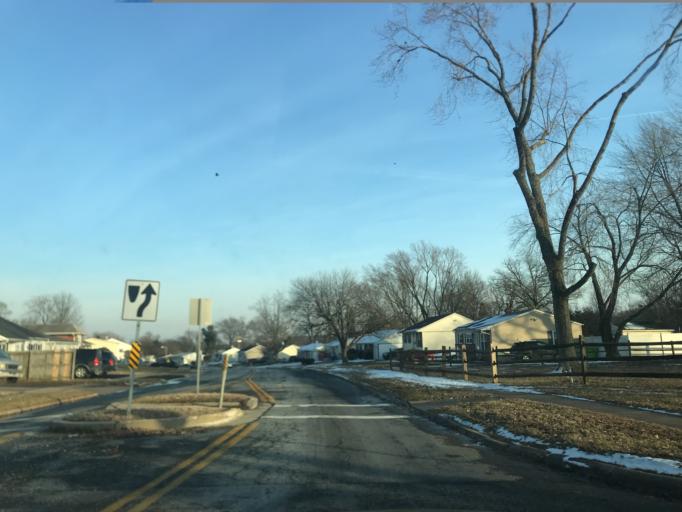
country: US
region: Maryland
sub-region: Harford County
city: Edgewood
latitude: 39.4251
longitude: -76.3046
